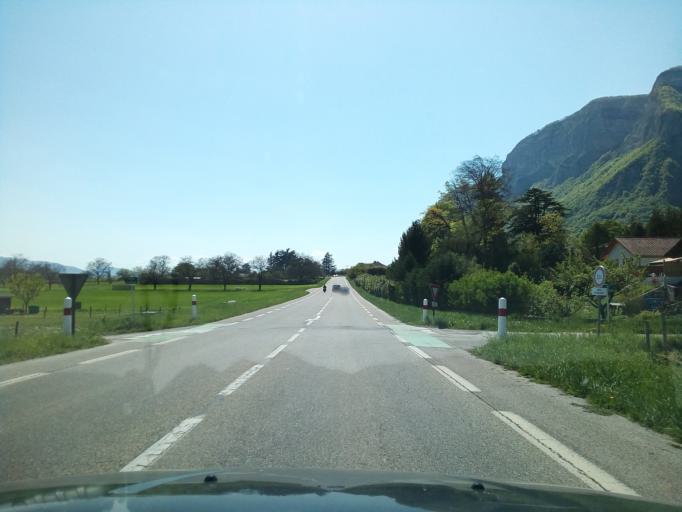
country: FR
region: Rhone-Alpes
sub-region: Departement de l'Isere
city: La Terrasse
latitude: 45.3209
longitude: 5.9300
